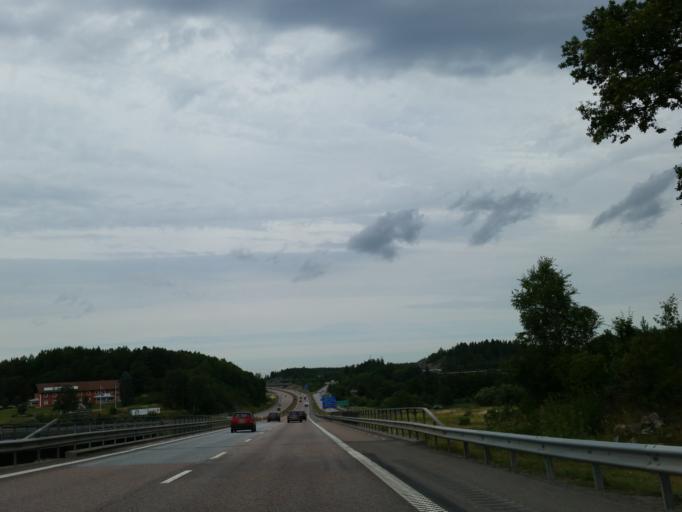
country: SE
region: Soedermanland
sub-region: Strangnas Kommun
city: Mariefred
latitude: 59.2402
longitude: 17.1795
